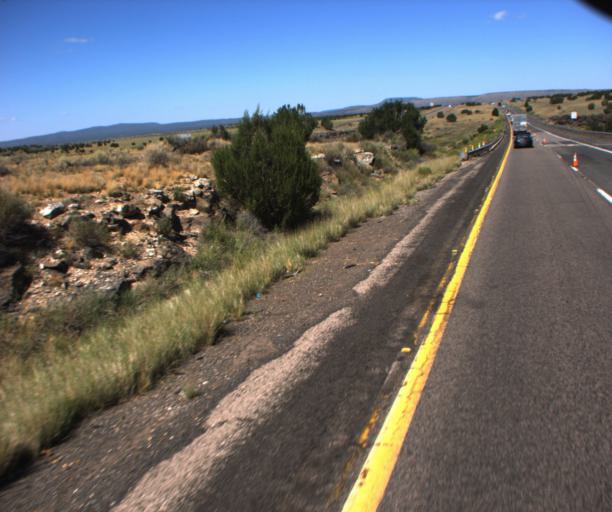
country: US
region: Arizona
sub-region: Mohave County
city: Peach Springs
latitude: 35.3222
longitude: -112.9046
